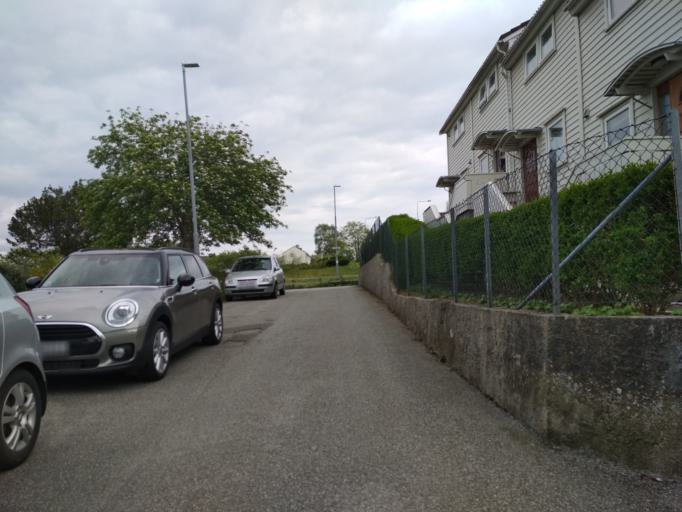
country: NO
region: Rogaland
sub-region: Stavanger
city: Stavanger
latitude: 58.9490
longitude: 5.7340
